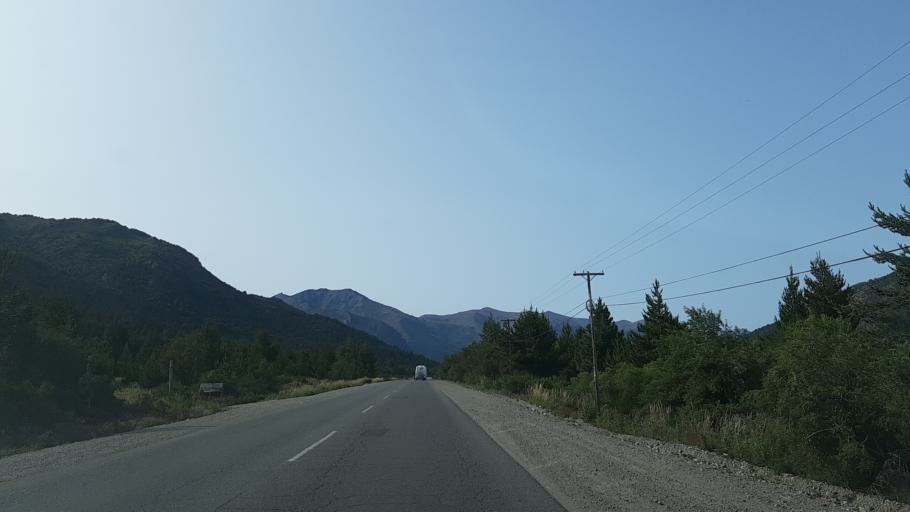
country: AR
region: Rio Negro
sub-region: Departamento de Bariloche
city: San Carlos de Bariloche
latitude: -41.1359
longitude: -71.4129
